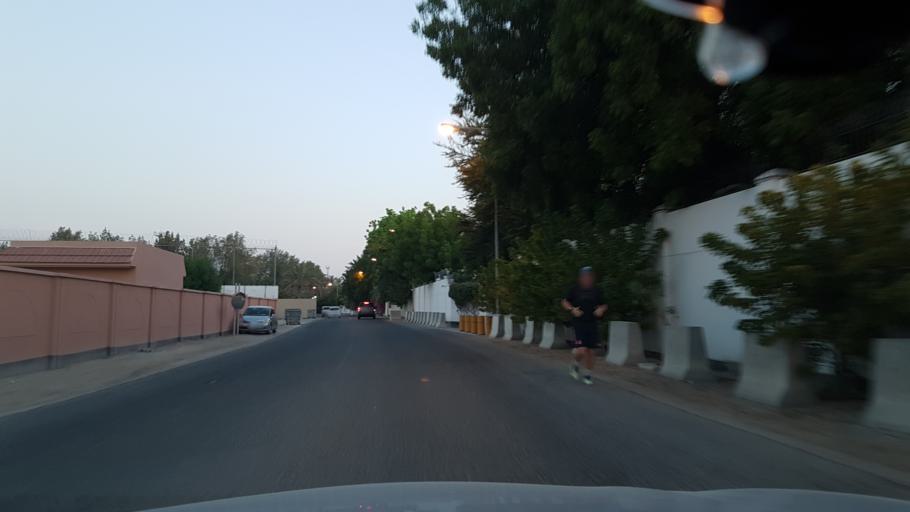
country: BH
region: Manama
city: Jidd Hafs
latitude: 26.2275
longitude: 50.4888
